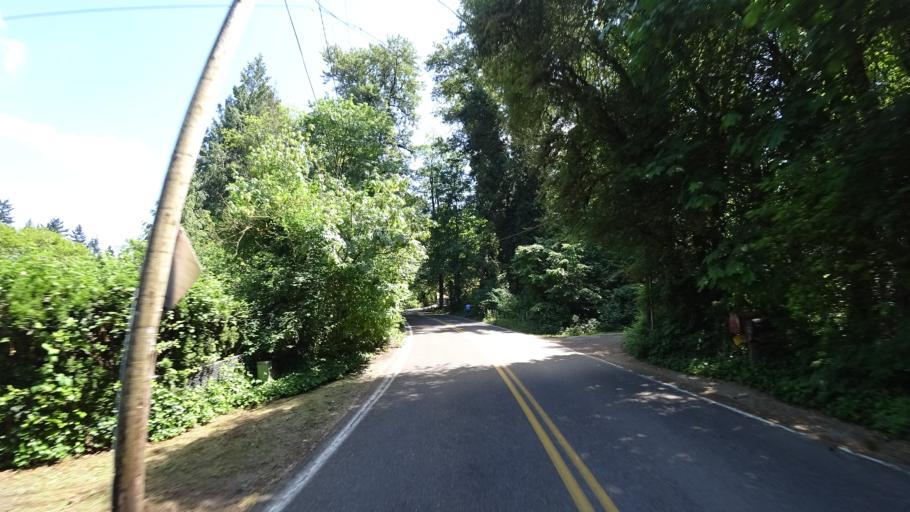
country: US
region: Oregon
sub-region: Clackamas County
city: Lake Oswego
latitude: 45.4450
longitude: -122.7011
